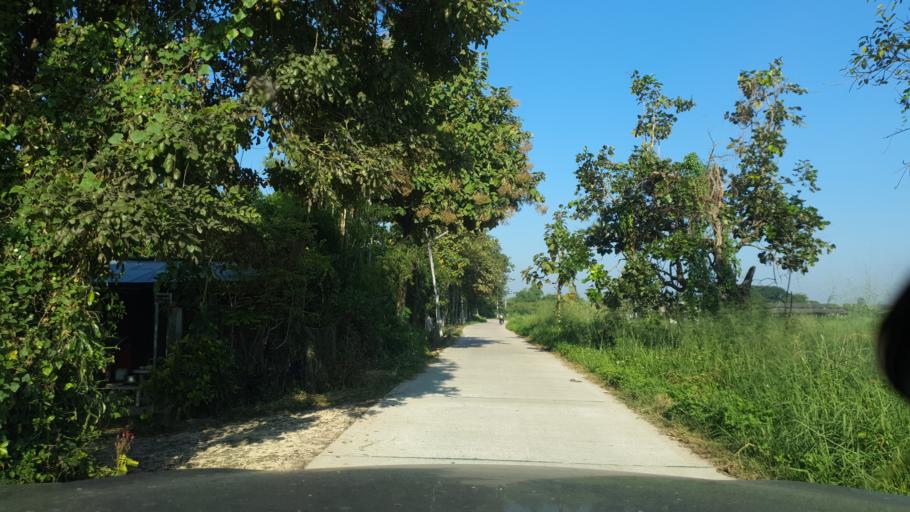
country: TH
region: Chiang Mai
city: San Kamphaeng
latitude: 18.6876
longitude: 99.1512
